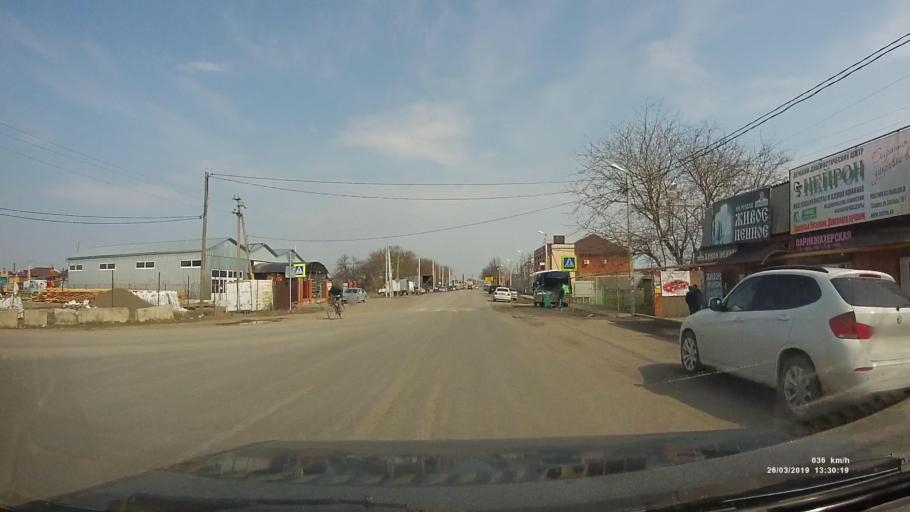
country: RU
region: Rostov
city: Novobessergenovka
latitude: 47.1818
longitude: 38.8196
